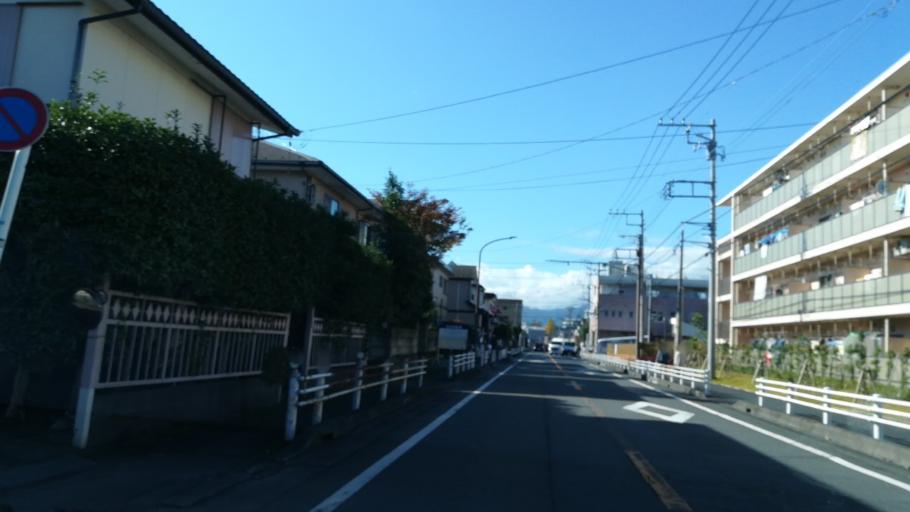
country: JP
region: Kanagawa
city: Zama
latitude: 35.5658
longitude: 139.3647
